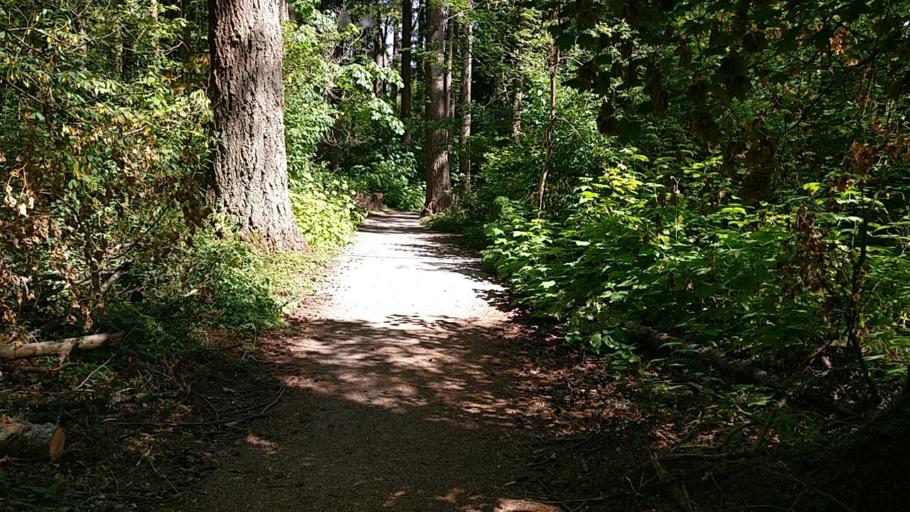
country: CA
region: British Columbia
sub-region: Greater Vancouver Regional District
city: White Rock
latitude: 49.0491
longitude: -122.8629
